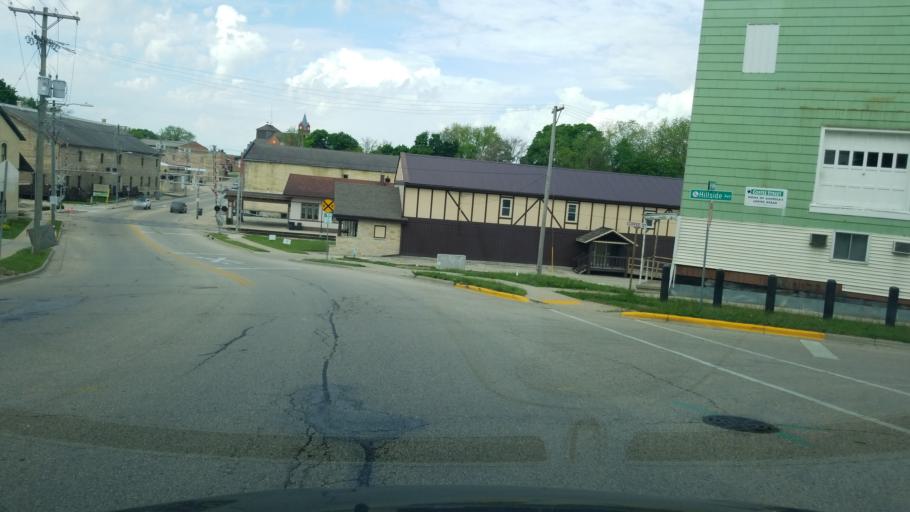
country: US
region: Wisconsin
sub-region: Dane County
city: Stoughton
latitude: 42.9185
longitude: -89.2134
